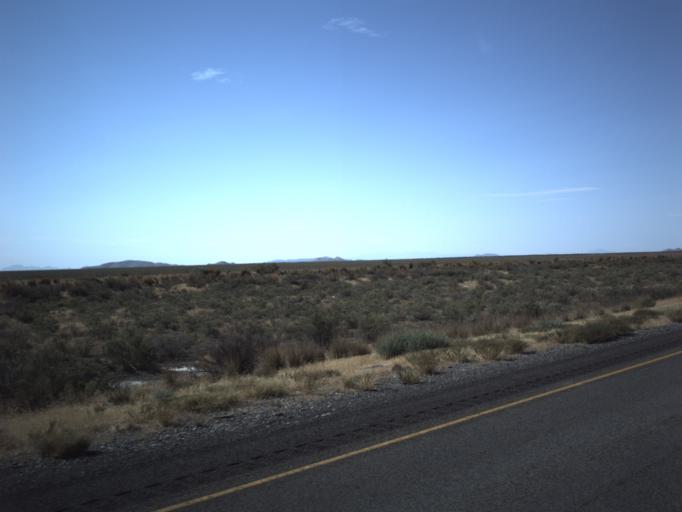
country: US
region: Utah
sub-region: Tooele County
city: Grantsville
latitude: 40.7409
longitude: -113.0832
